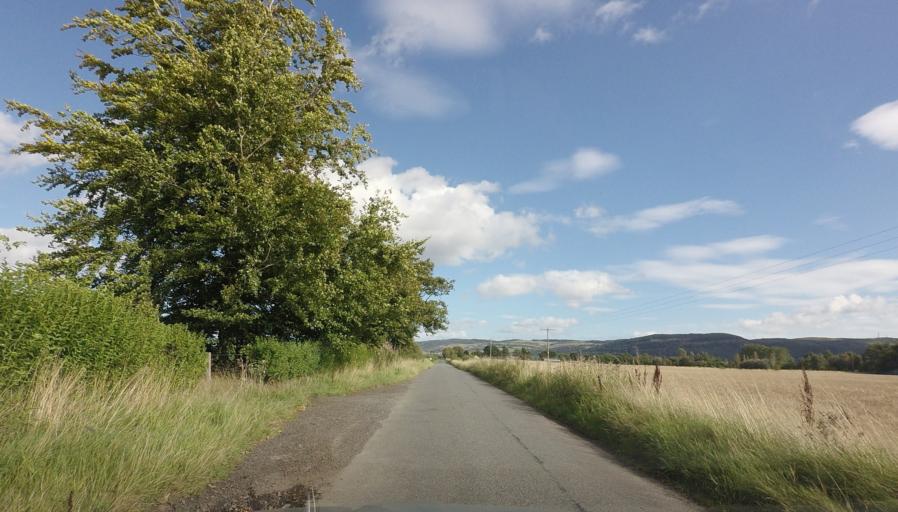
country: GB
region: Scotland
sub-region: Perth and Kinross
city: Bridge of Earn
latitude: 56.3454
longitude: -3.3858
